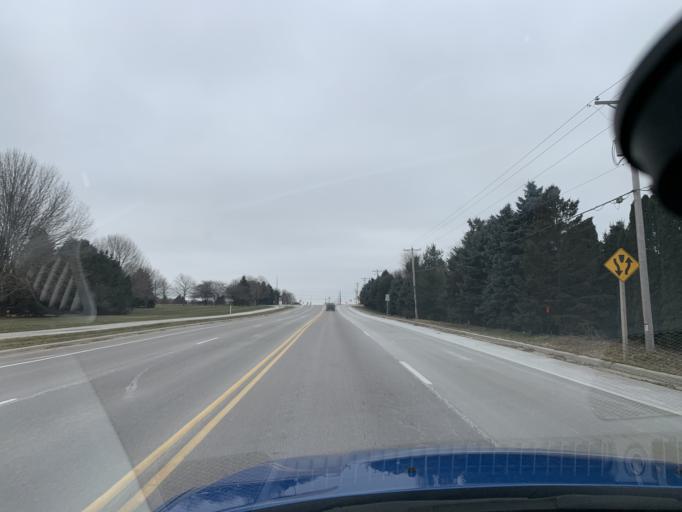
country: US
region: Wisconsin
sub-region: Dane County
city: Sun Prairie
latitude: 43.1907
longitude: -89.2644
